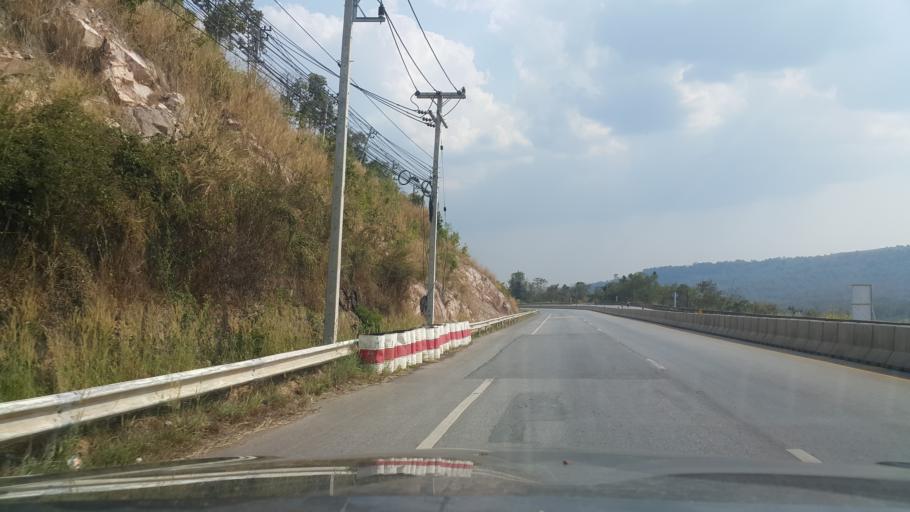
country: TH
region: Phitsanulok
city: Wang Thong
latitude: 16.8526
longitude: 100.5153
